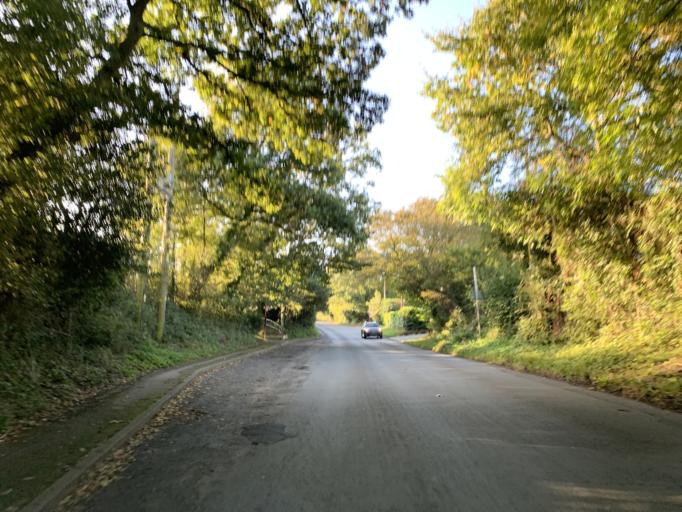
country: GB
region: England
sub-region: Wiltshire
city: Whiteparish
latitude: 50.9748
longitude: -1.6384
